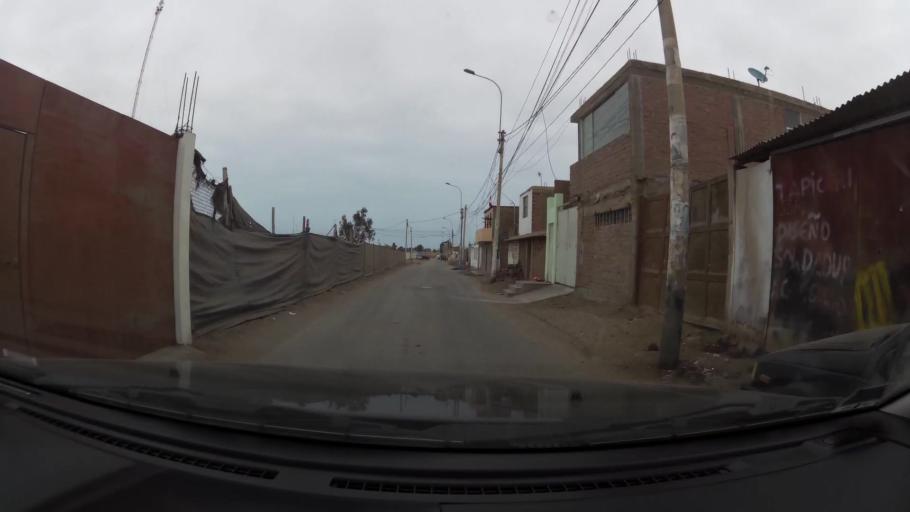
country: PE
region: Lima
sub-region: Provincia de Canete
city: Chilca
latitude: -12.5119
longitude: -76.7386
